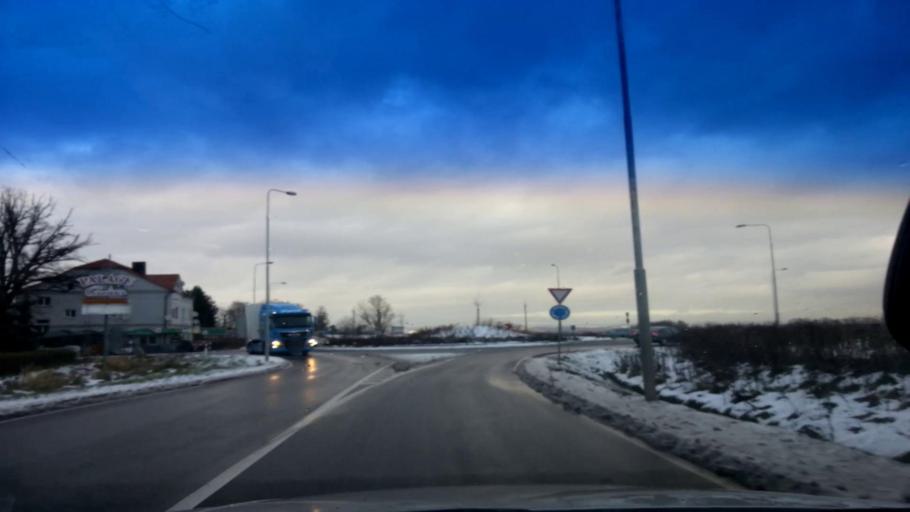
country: CZ
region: Karlovarsky
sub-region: Okres Cheb
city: Cheb
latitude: 50.0495
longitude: 12.3544
